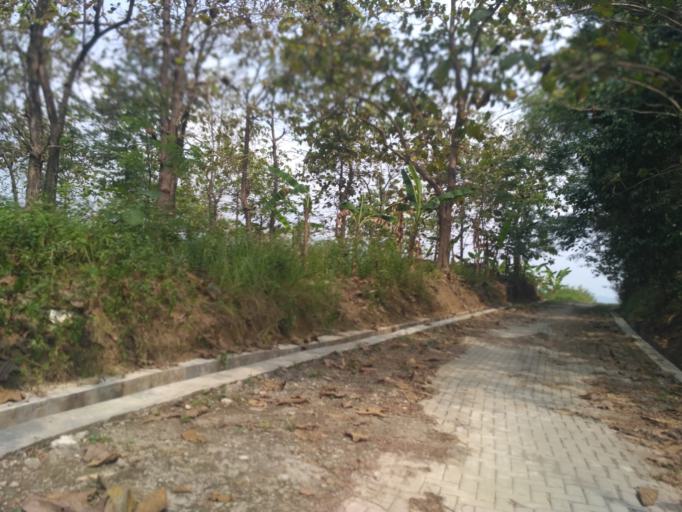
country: ID
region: Central Java
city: Mranggen
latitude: -7.0672
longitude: 110.4637
